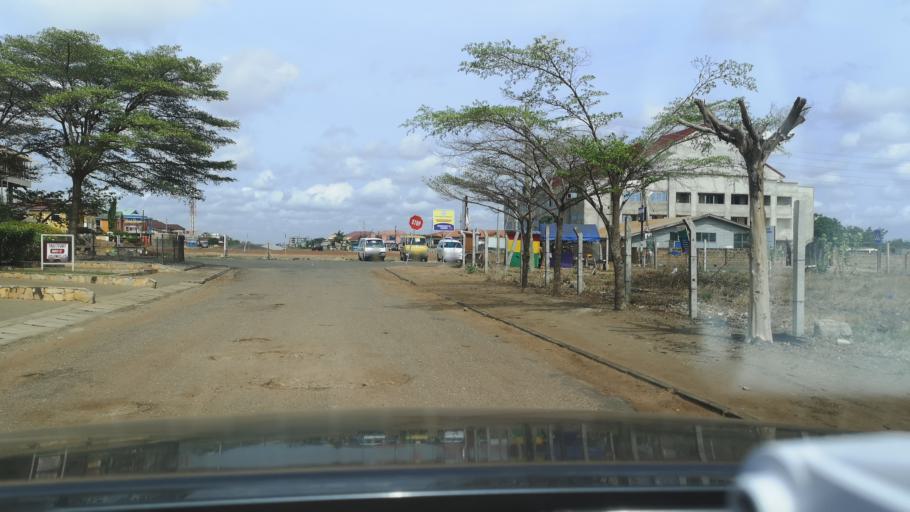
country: GH
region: Greater Accra
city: Nungua
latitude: 5.6504
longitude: -0.0759
